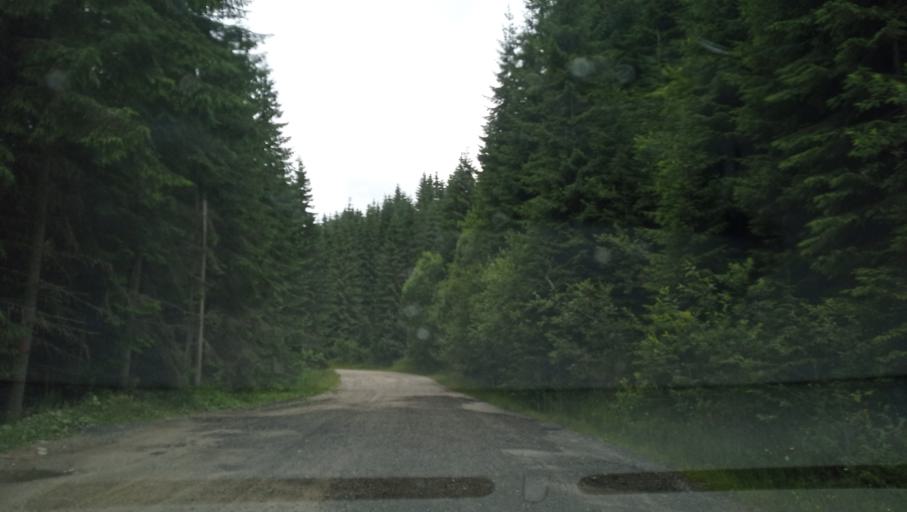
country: RO
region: Valcea
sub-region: Comuna Voineasa
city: Voineasa
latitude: 45.4251
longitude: 23.7632
